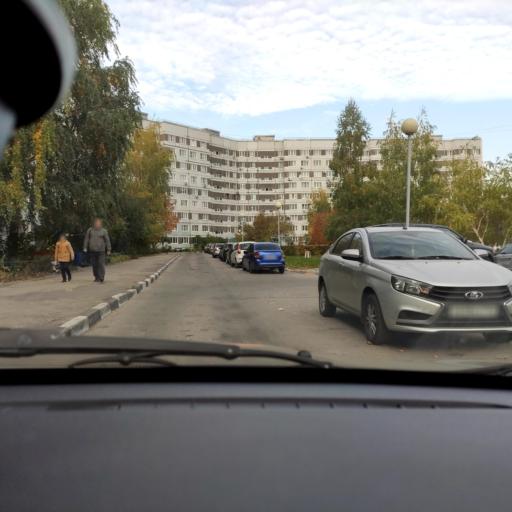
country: RU
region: Samara
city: Tol'yatti
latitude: 53.5339
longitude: 49.3317
